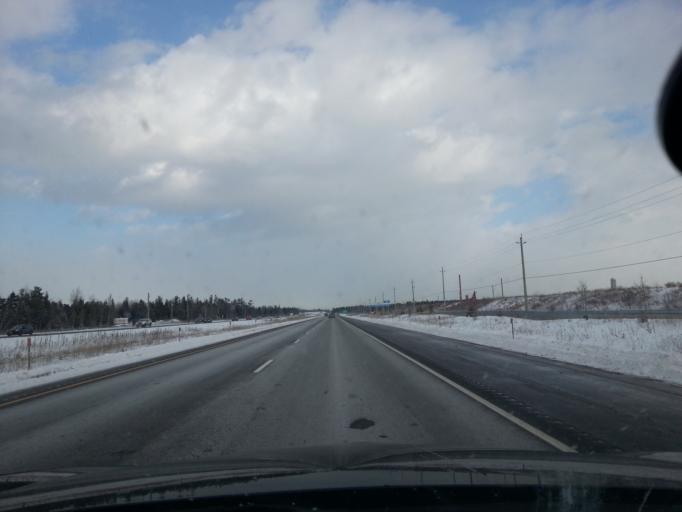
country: CA
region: Ontario
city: Bells Corners
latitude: 45.2347
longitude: -75.9872
